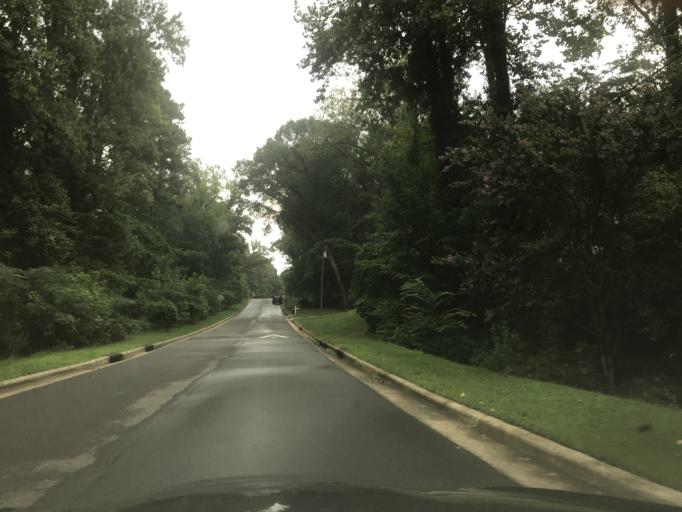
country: US
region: North Carolina
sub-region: Wake County
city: West Raleigh
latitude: 35.8354
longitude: -78.6619
